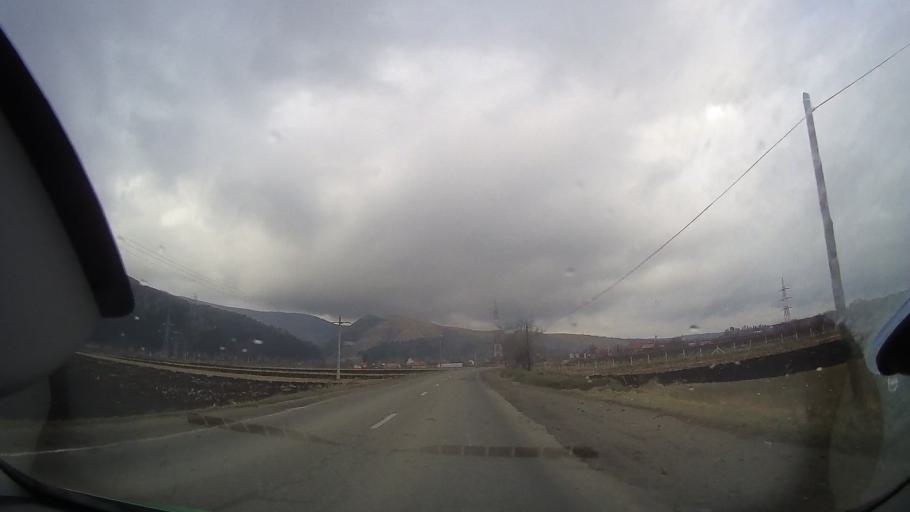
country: RO
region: Cluj
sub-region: Comuna Moldovenesti
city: Moldovenesti
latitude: 46.5155
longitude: 23.6800
